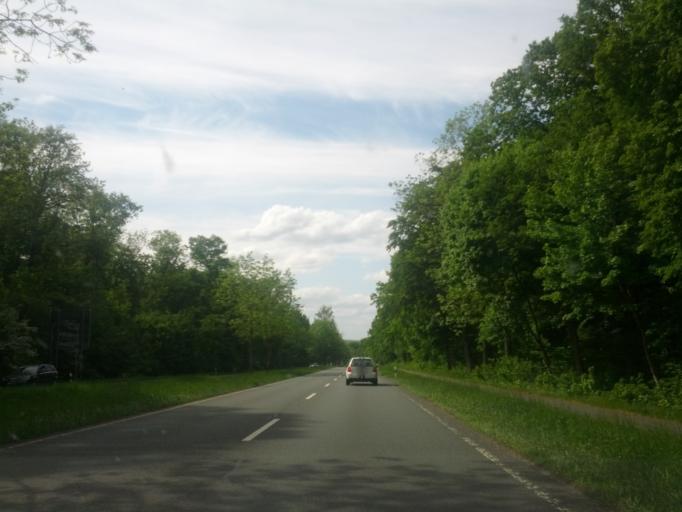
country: DE
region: Thuringia
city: Erfurt
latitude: 50.9445
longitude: 11.0327
